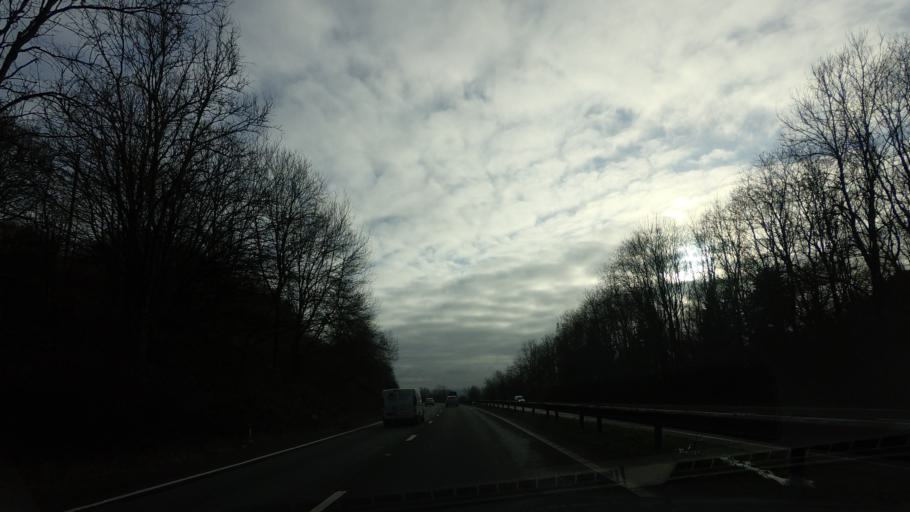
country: GB
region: England
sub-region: Kent
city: Sevenoaks
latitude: 51.2495
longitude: 0.1785
